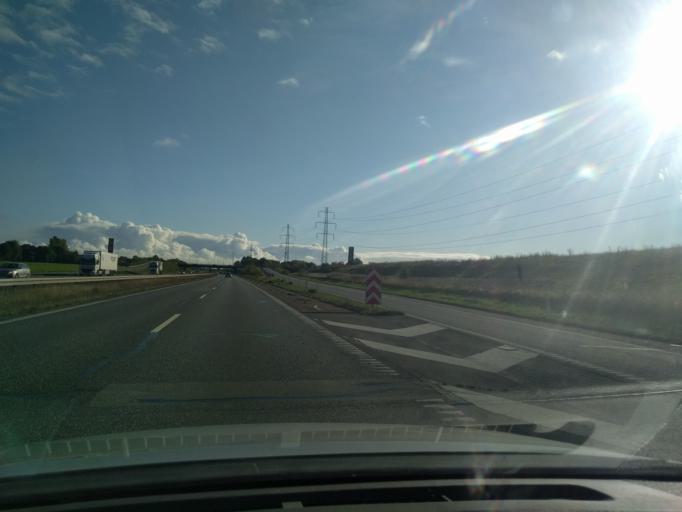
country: DK
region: Zealand
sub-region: Ringsted Kommune
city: Ringsted
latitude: 55.4548
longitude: 11.7826
